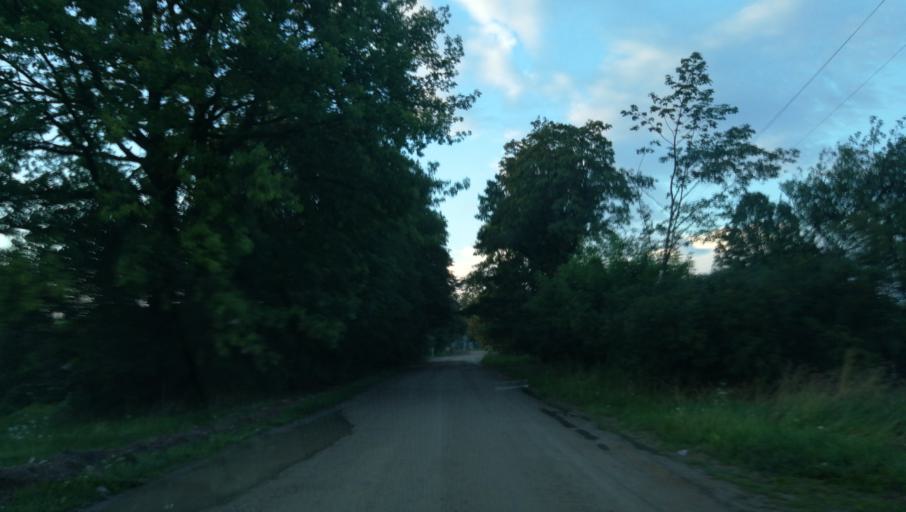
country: LV
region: Cesu Rajons
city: Cesis
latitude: 57.3185
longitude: 25.2960
